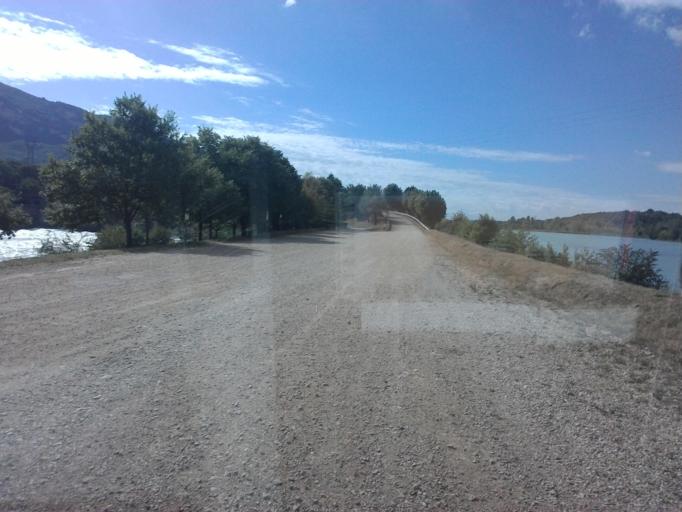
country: FR
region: Rhone-Alpes
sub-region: Departement de l'Ain
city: Sault-Brenaz
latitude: 45.8468
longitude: 5.4157
